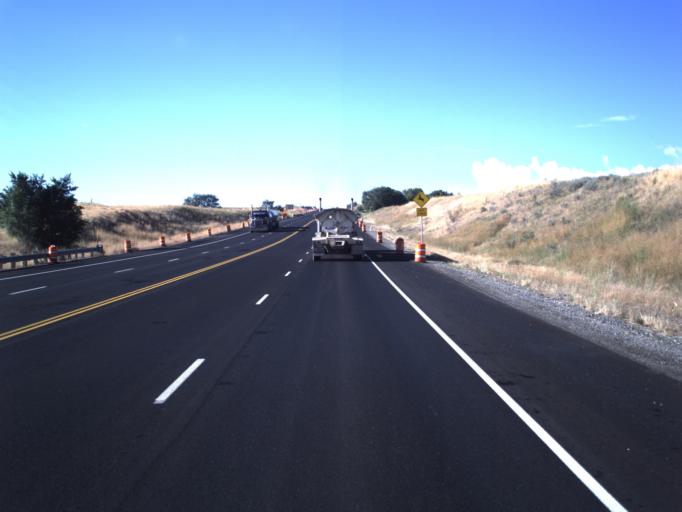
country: US
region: Utah
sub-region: Salt Lake County
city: Magna
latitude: 40.6781
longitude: -112.0920
